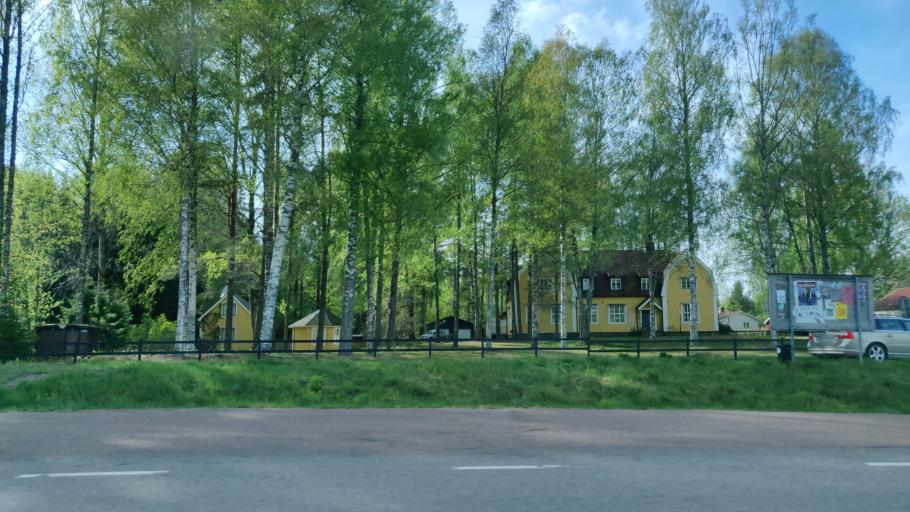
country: SE
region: Vaermland
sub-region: Forshaga Kommun
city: Forshaga
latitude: 59.5163
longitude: 13.4435
